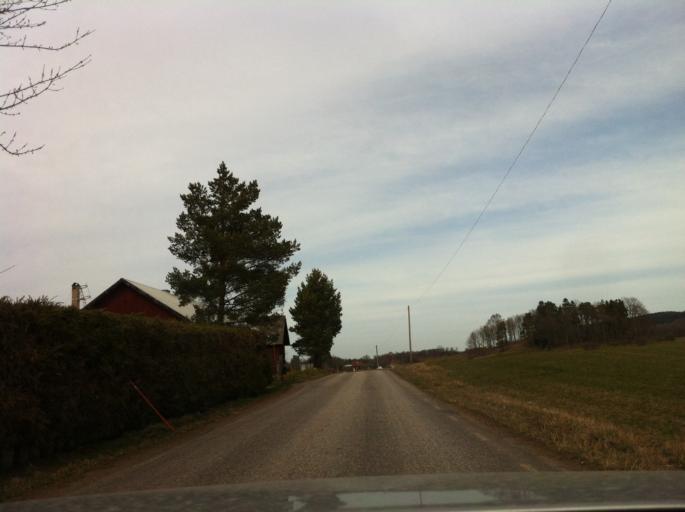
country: SE
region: Vaestra Goetaland
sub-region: Skara Kommun
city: Axvall
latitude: 58.4021
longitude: 13.6620
